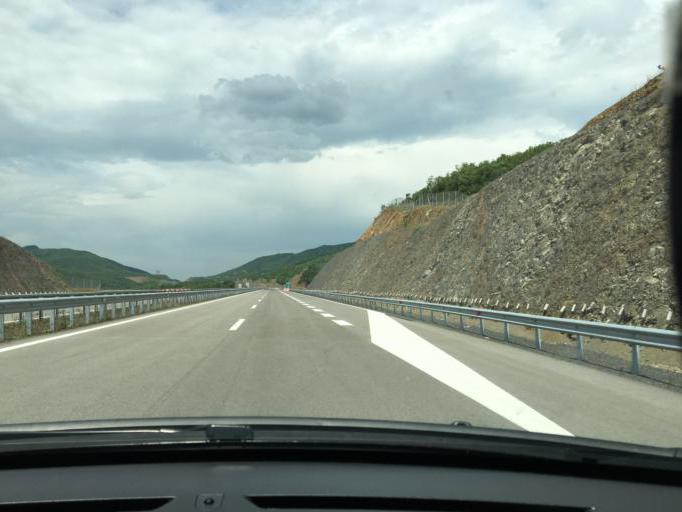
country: MK
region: Gevgelija
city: Miravci
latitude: 41.3212
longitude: 22.4048
